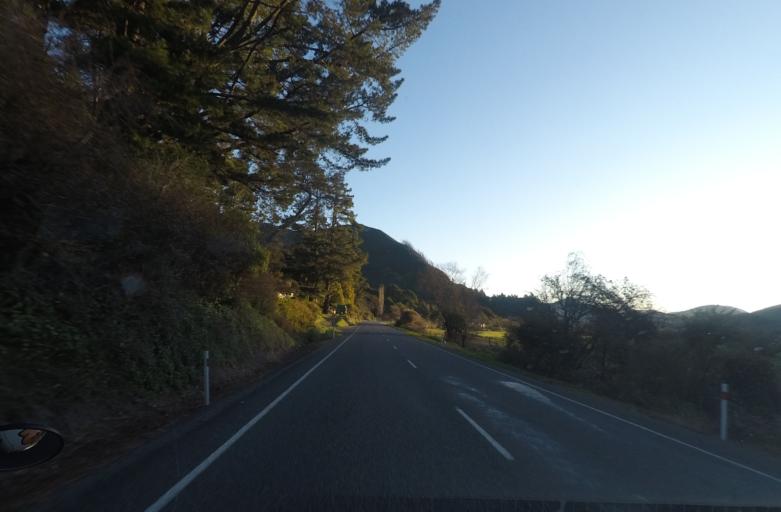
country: NZ
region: Marlborough
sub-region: Marlborough District
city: Picton
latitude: -41.2876
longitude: 173.7050
